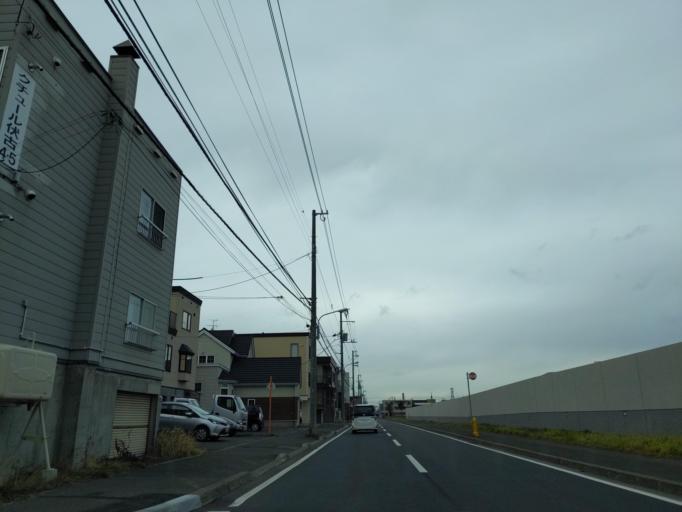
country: JP
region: Hokkaido
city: Sapporo
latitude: 43.0841
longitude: 141.3954
